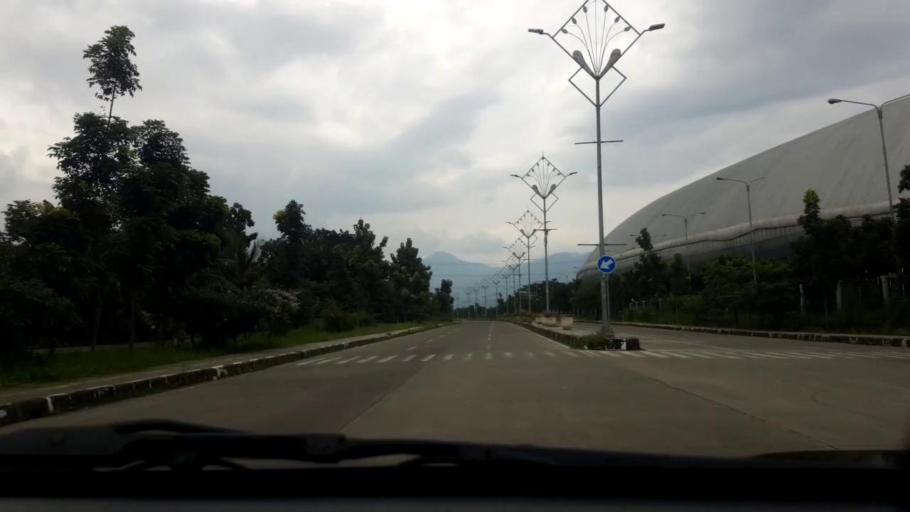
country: ID
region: West Java
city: Cileunyi
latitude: -6.9591
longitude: 107.7103
